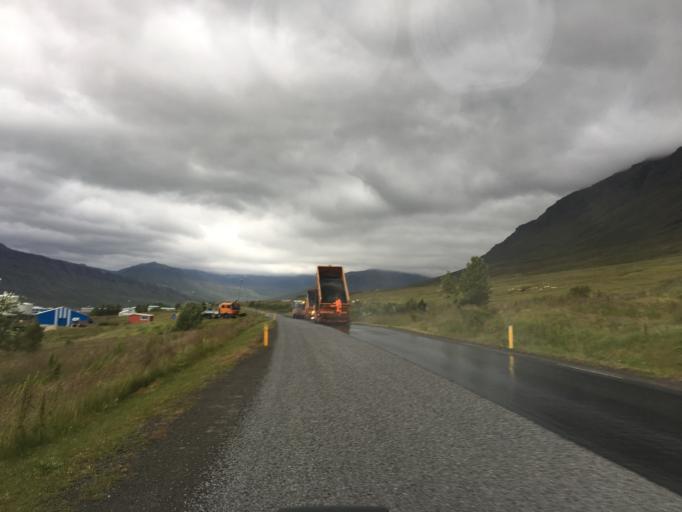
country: IS
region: East
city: Neskaupstadur
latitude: 65.1453
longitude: -13.7287
